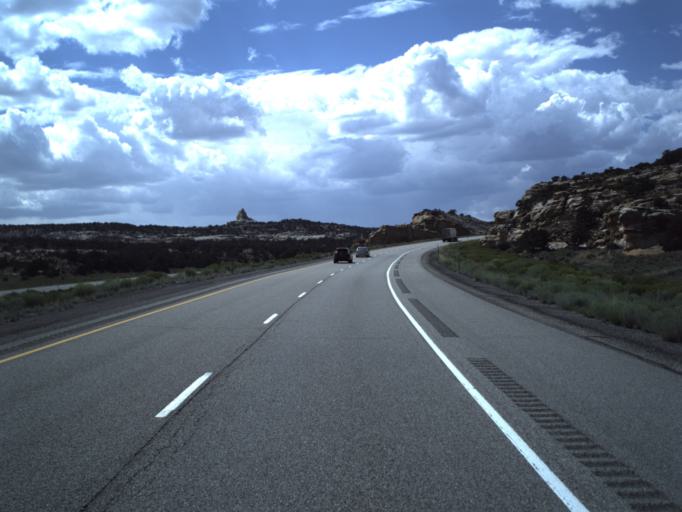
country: US
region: Utah
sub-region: Emery County
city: Ferron
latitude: 38.8652
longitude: -110.7929
